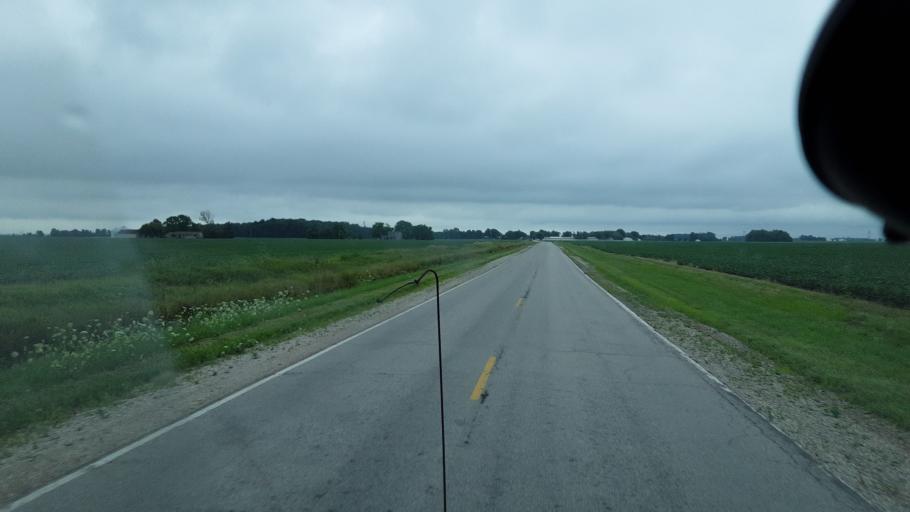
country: US
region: Indiana
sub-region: Wells County
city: Bluffton
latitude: 40.7919
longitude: -85.0908
